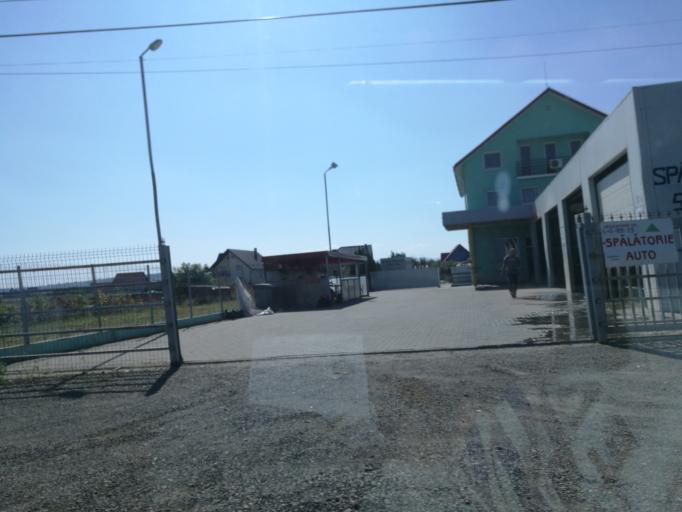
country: RO
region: Suceava
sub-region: Municipiul Suceava
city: Radauti
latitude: 47.8298
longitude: 25.9357
